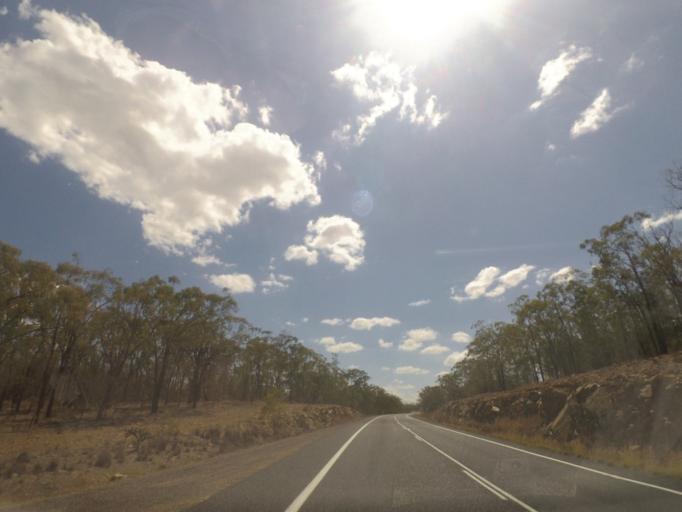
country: AU
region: Queensland
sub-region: Southern Downs
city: Warwick
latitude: -28.1628
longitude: 151.6813
